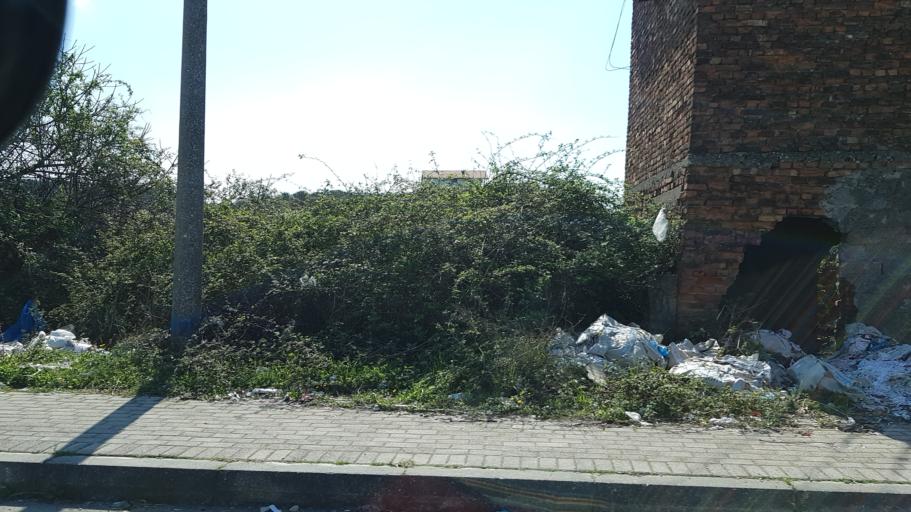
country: AL
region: Shkoder
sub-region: Rrethi i Shkodres
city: Shkoder
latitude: 42.0545
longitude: 19.5187
